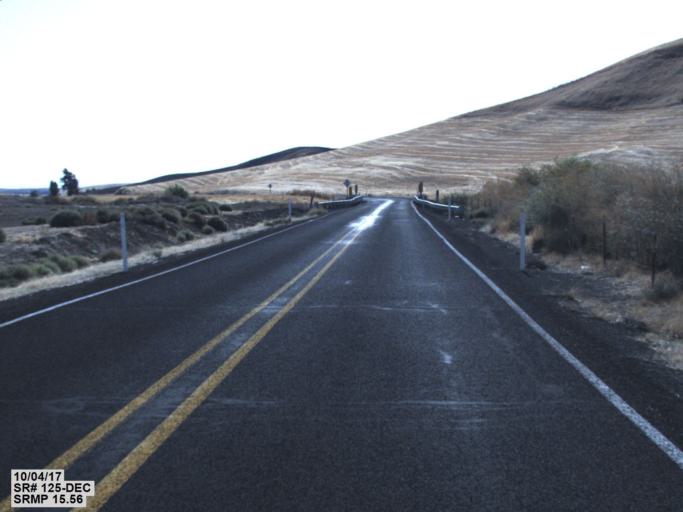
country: US
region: Washington
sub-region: Walla Walla County
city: Walla Walla
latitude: 46.1939
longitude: -118.3826
